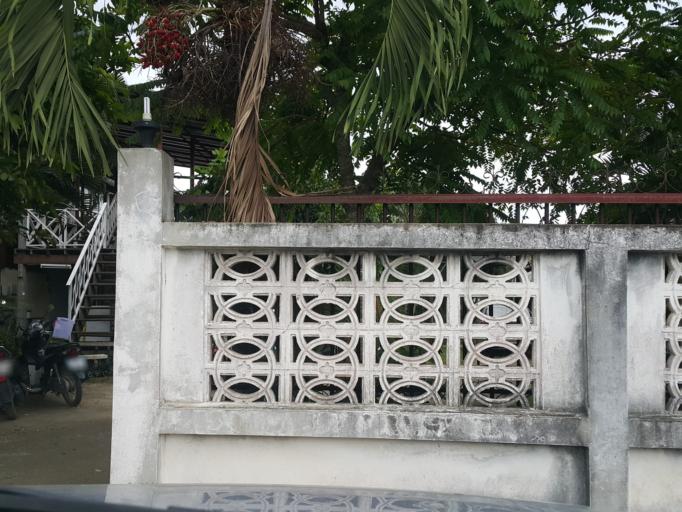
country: TH
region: Chiang Mai
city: San Kamphaeng
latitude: 18.7973
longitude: 99.1419
